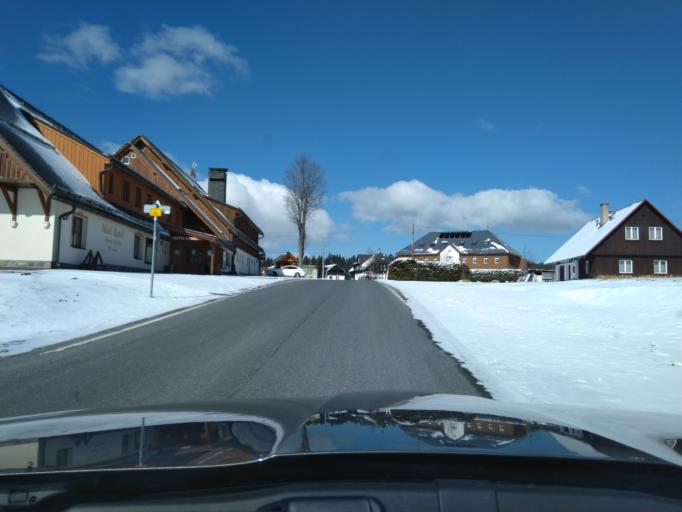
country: CZ
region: Plzensky
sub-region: Okres Klatovy
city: Kasperske Hory
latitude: 49.0575
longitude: 13.5589
